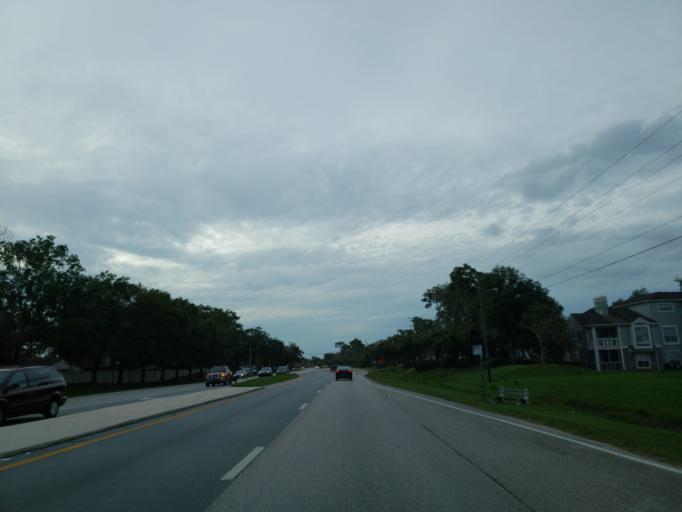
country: US
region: Florida
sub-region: Hillsborough County
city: Carrollwood Village
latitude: 28.0591
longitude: -82.5360
